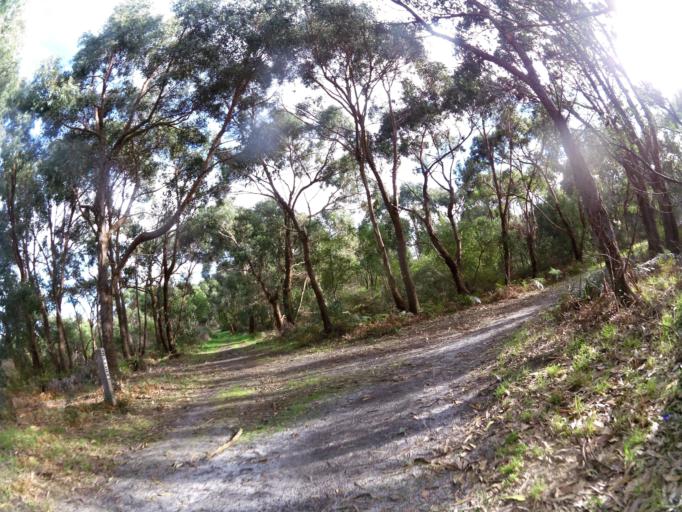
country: AU
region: Victoria
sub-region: Bass Coast
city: North Wonthaggi
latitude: -38.6239
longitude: 145.5723
